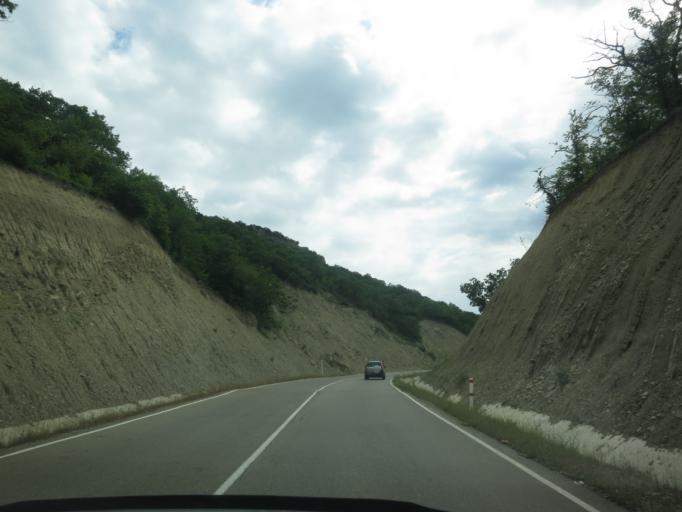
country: GE
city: Didi Lilo
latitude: 41.8096
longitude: 45.1430
